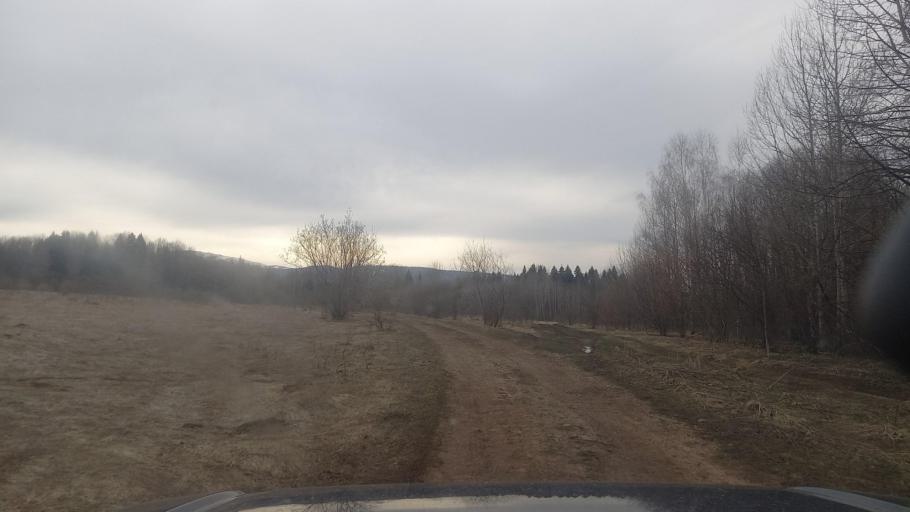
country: RU
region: Adygeya
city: Kamennomostskiy
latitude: 44.1653
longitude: 40.0230
